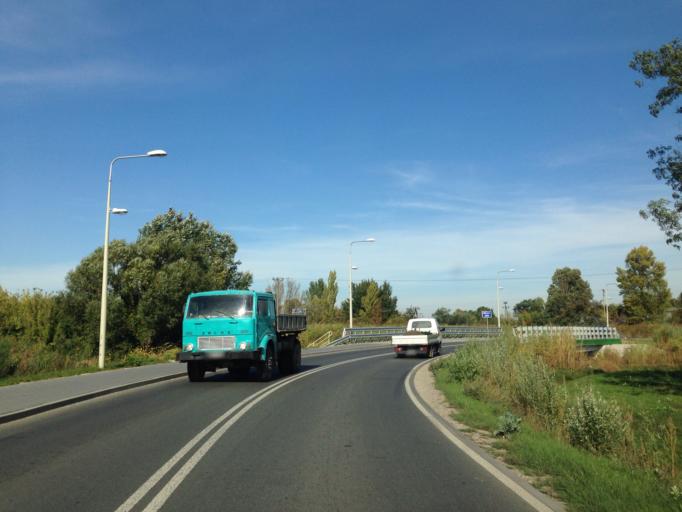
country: PL
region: Masovian Voivodeship
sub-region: Powiat warszawski zachodni
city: Ozarow Mazowiecki
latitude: 52.1792
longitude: 20.7733
